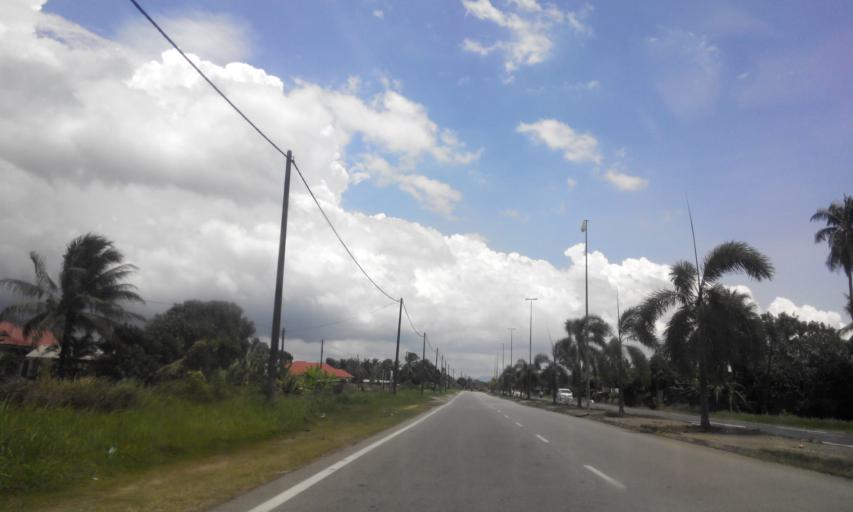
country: MY
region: Perak
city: Parit Buntar
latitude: 5.1229
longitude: 100.5176
